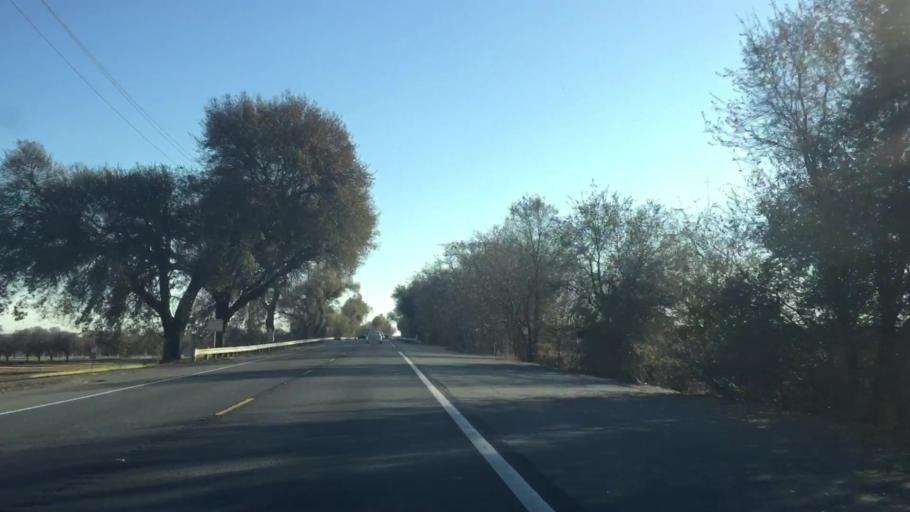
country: US
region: California
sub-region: Sutter County
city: Live Oak
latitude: 39.3174
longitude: -121.5959
